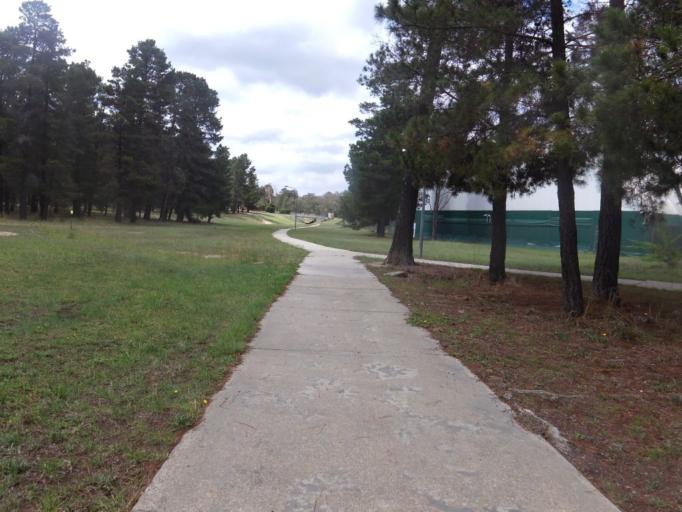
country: AU
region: Australian Capital Territory
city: Macarthur
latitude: -35.4112
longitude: 149.1267
